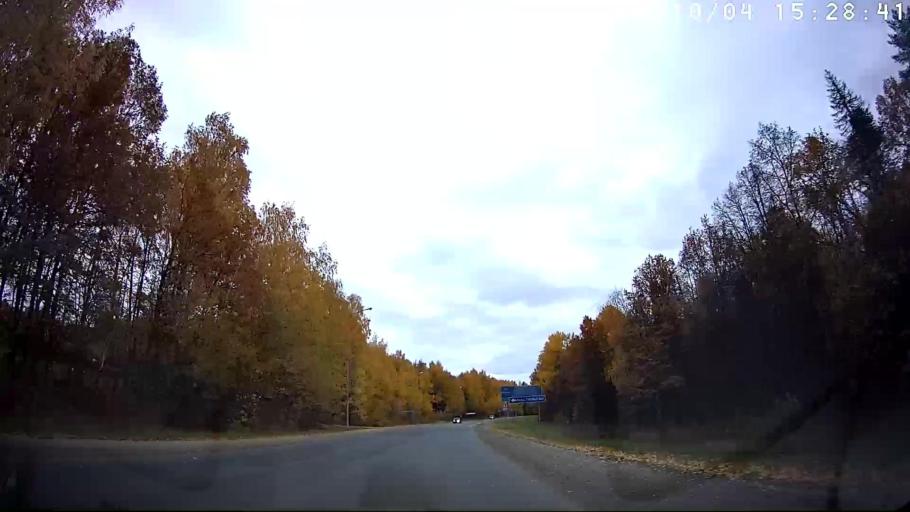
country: RU
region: Mariy-El
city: Yoshkar-Ola
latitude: 56.6073
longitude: 47.9683
